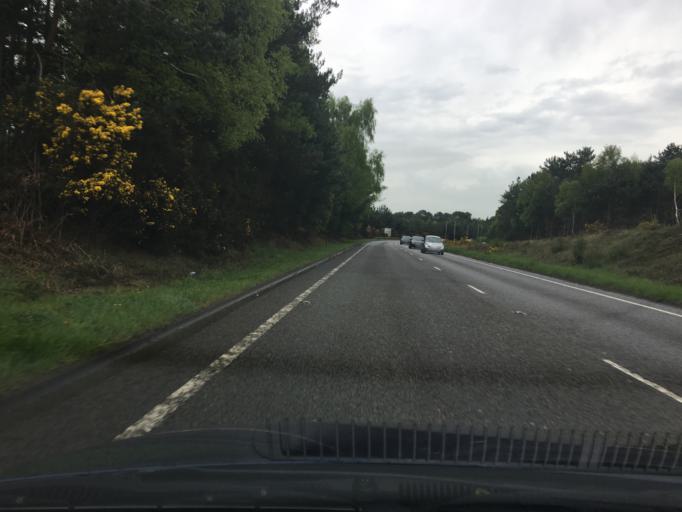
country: GB
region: England
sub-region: Bracknell Forest
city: Crowthorne
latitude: 51.3790
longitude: -0.7717
